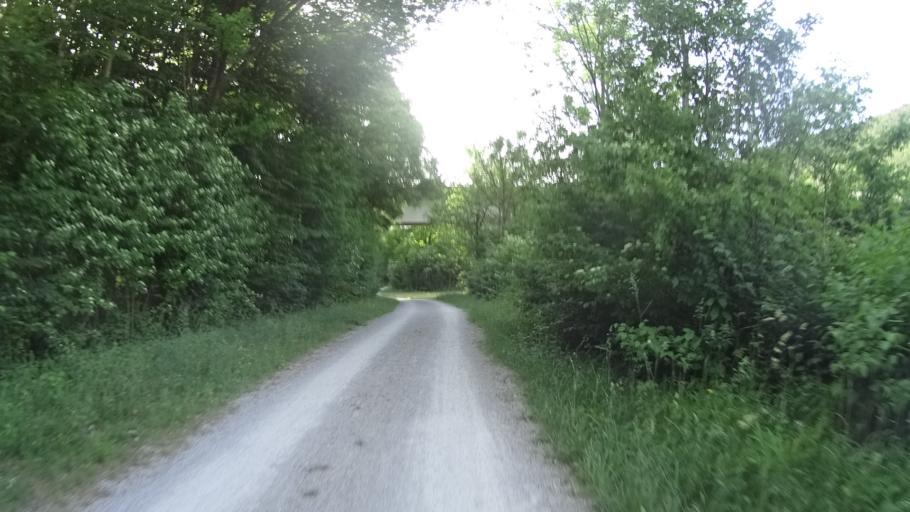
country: DE
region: Bavaria
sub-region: Lower Bavaria
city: Essing
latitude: 48.9465
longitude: 11.7421
